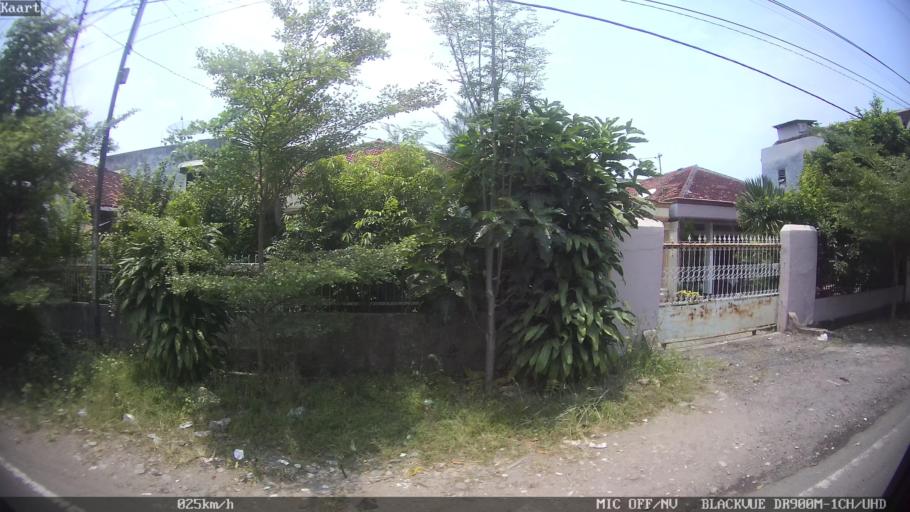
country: ID
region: Lampung
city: Bandarlampung
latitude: -5.4408
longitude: 105.2740
